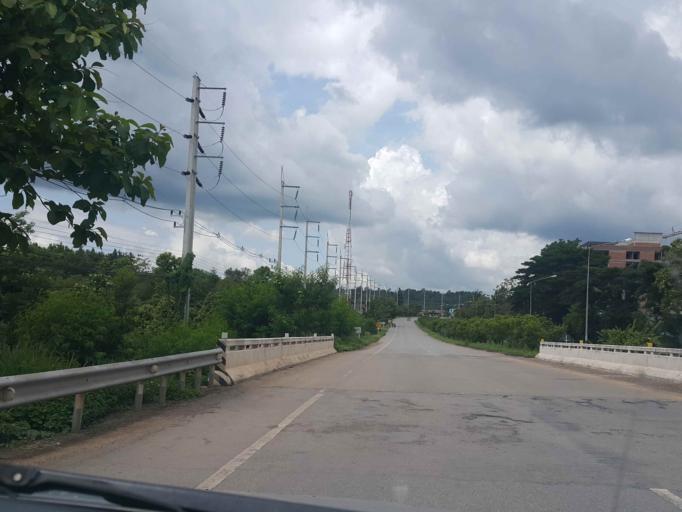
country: TH
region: Phayao
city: Dok Kham Tai
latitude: 19.0242
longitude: 99.9220
